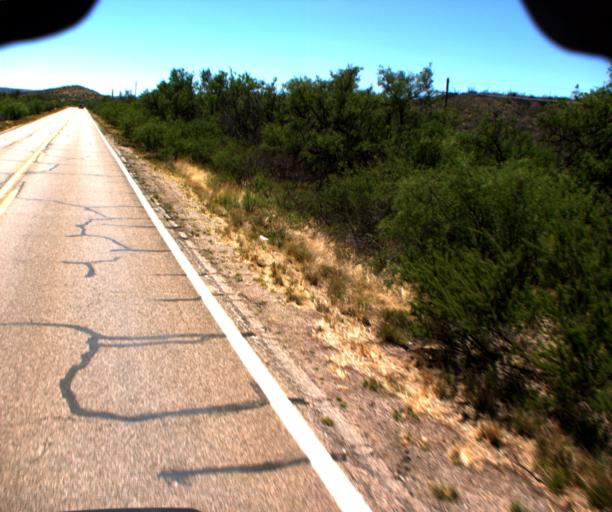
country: US
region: Arizona
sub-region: Pima County
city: Corona de Tucson
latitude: 31.9164
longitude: -110.6584
